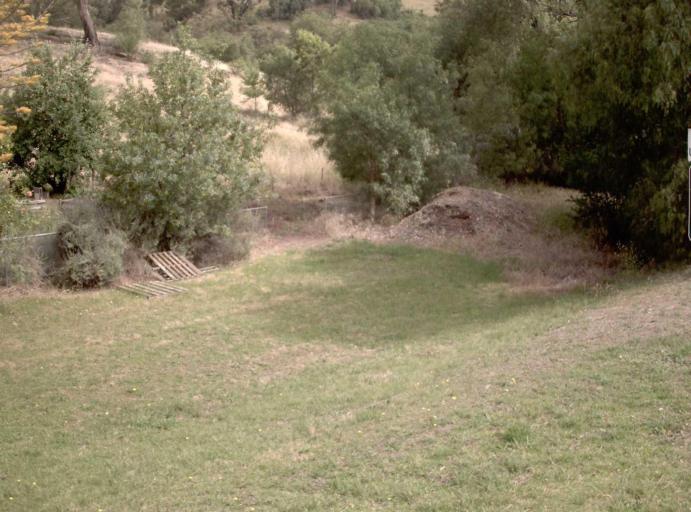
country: AU
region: Victoria
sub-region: Wellington
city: Heyfield
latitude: -37.6272
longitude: 146.6236
